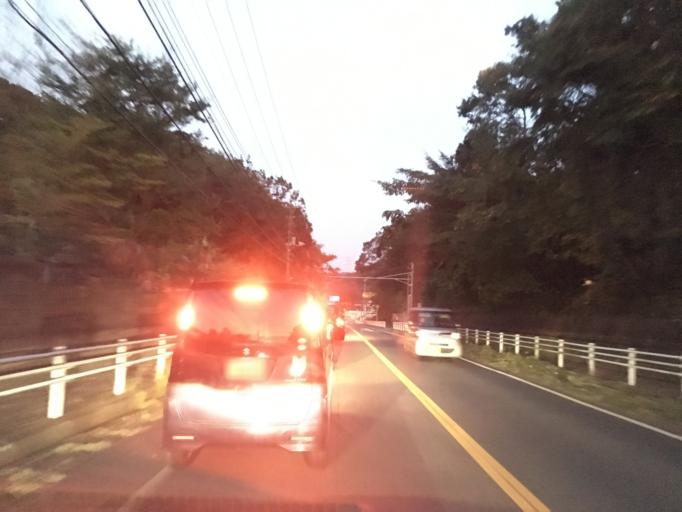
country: JP
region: Chiba
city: Kisarazu
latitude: 35.3447
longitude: 139.9184
